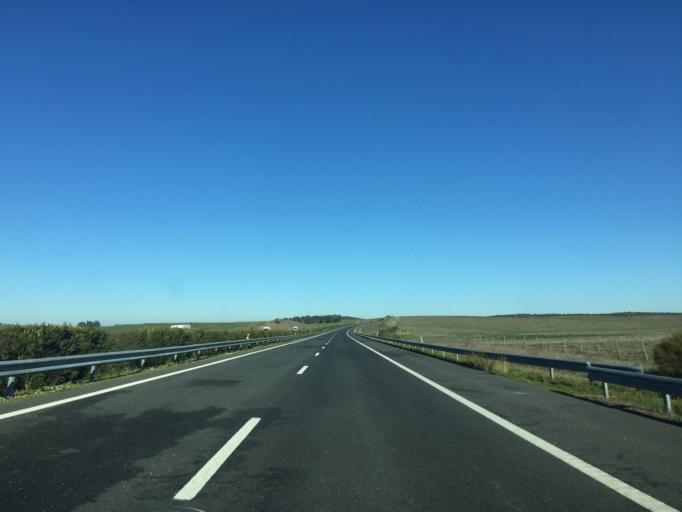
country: PT
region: Beja
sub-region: Aljustrel
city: Aljustrel
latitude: 37.7928
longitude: -8.2218
